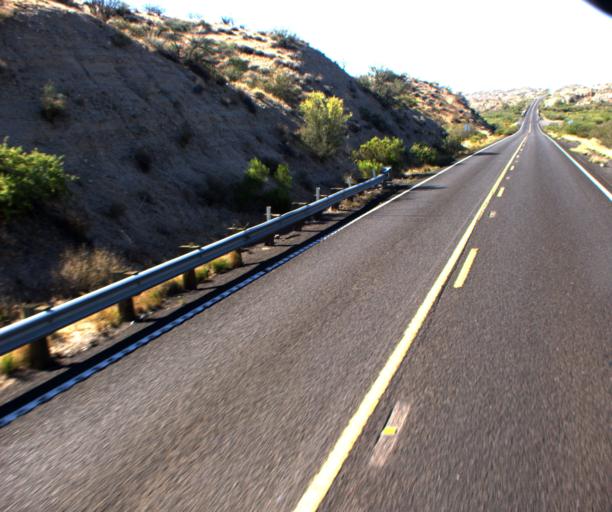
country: US
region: Arizona
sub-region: Mohave County
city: Kingman
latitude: 34.9228
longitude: -113.6582
